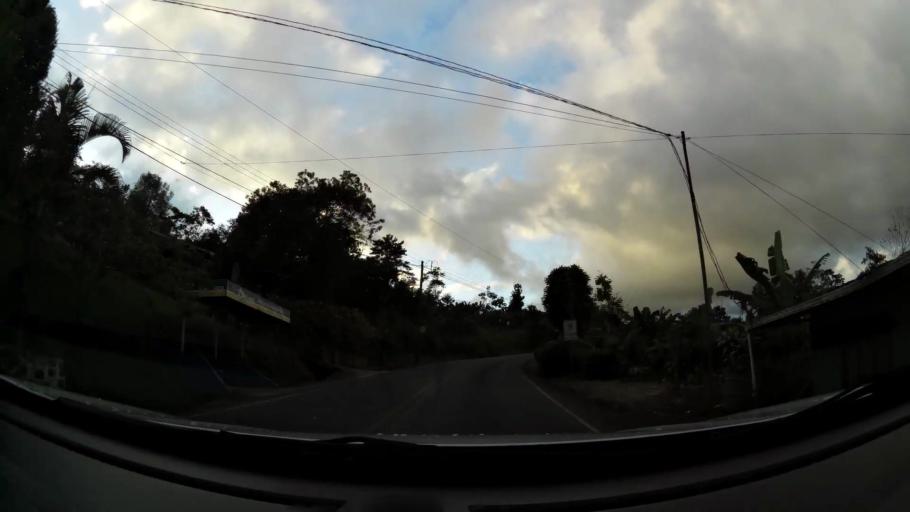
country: CR
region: Cartago
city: Turrialba
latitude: 9.8990
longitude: -83.6927
